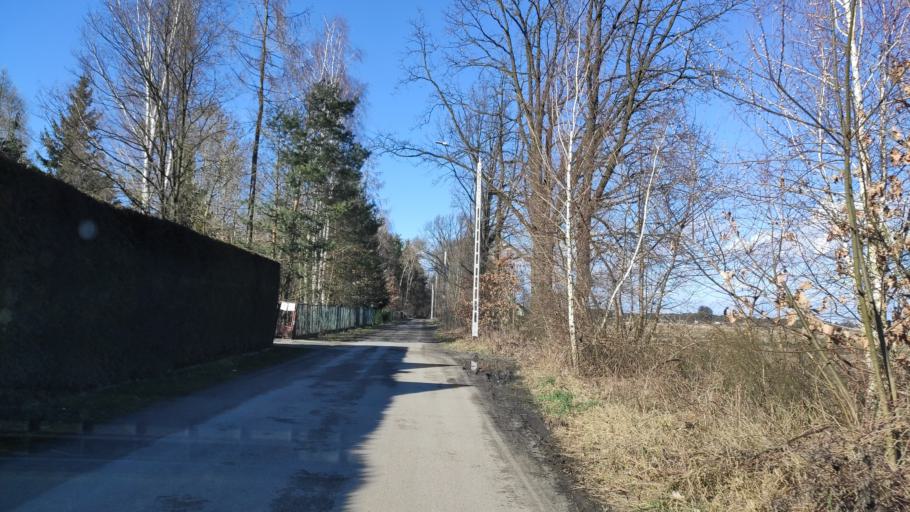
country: PL
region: Masovian Voivodeship
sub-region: Powiat radomski
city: Jedlnia-Letnisko
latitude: 51.4492
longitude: 21.3265
